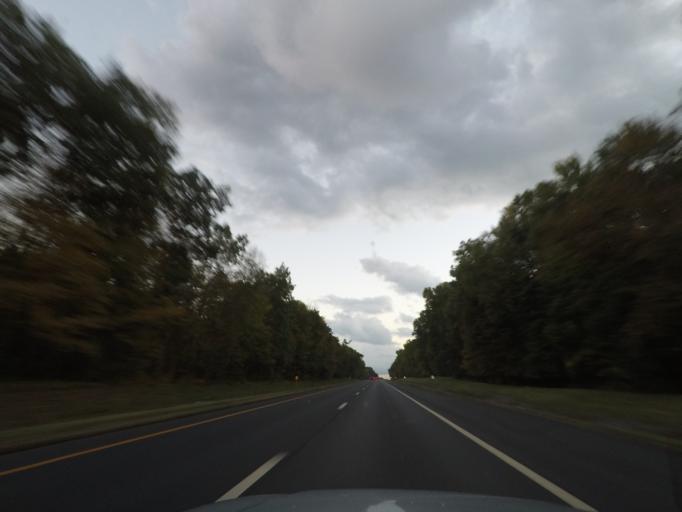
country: US
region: New York
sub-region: Ulster County
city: New Paltz
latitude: 41.7804
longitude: -74.0512
